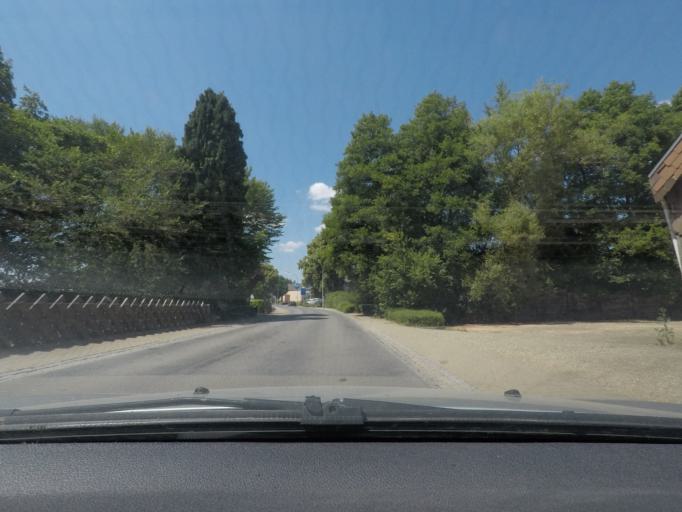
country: LU
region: Diekirch
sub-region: Canton de Redange
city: Redange-sur-Attert
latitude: 49.7649
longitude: 5.8810
